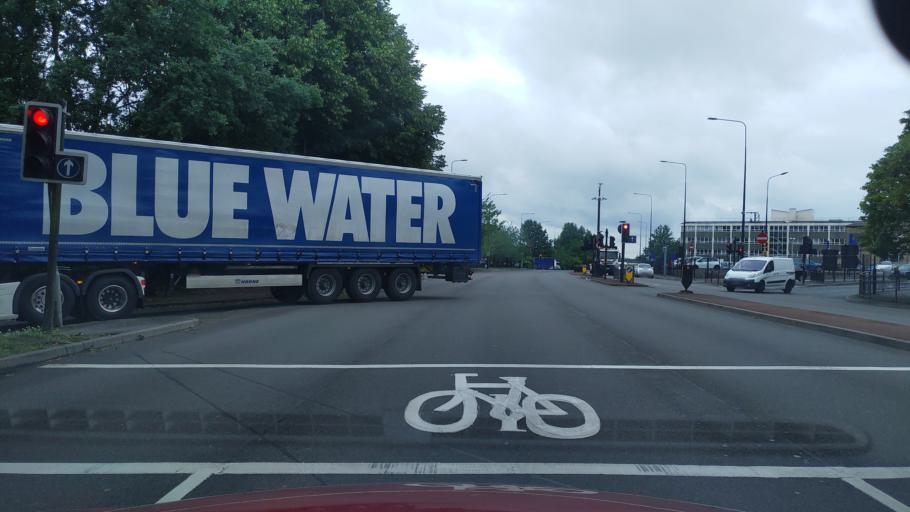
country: GB
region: England
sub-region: Borough of Wigan
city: Ince-in-Makerfield
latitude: 53.5448
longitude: -2.6279
